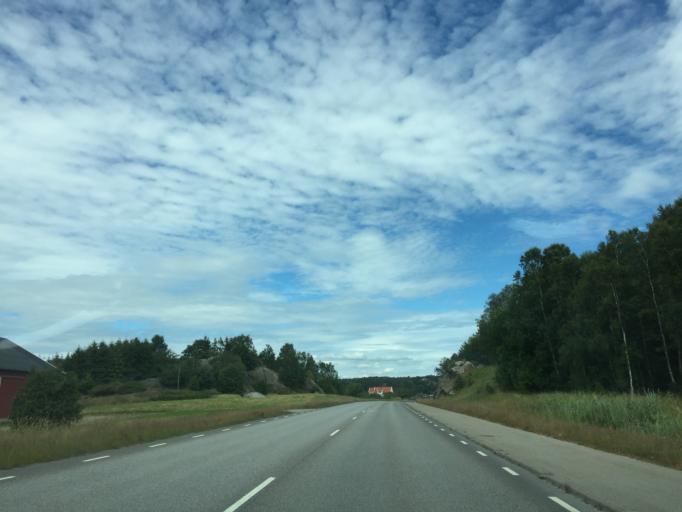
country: SE
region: Vaestra Goetaland
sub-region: Tjorns Kommun
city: Skaerhamn
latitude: 58.0141
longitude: 11.6121
